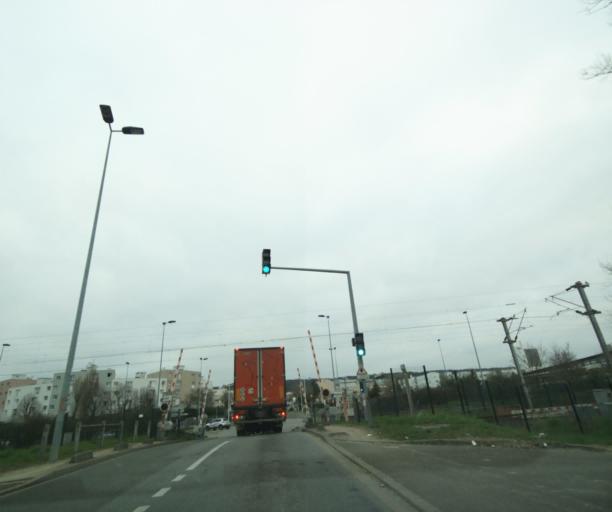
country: FR
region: Ile-de-France
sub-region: Departement des Yvelines
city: Chanteloup-les-Vignes
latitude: 48.9697
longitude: 2.0323
